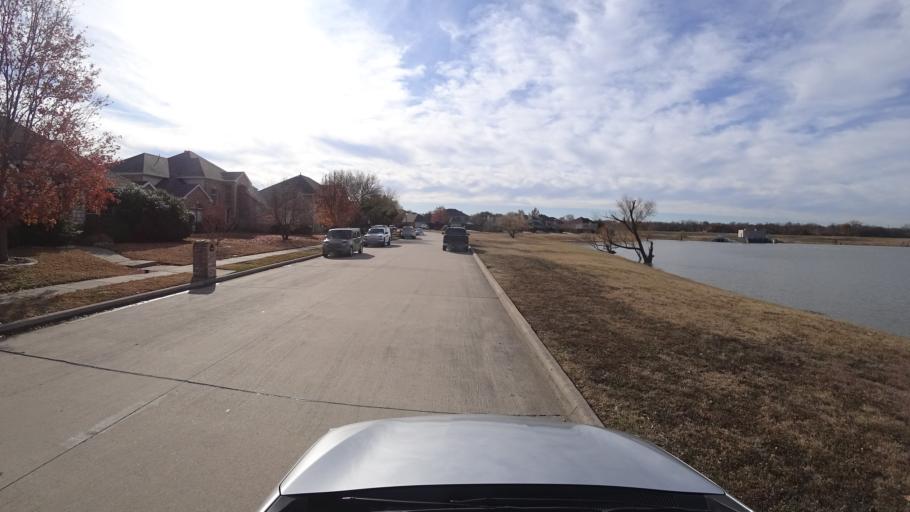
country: US
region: Texas
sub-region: Denton County
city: Lewisville
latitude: 33.0093
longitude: -96.9377
